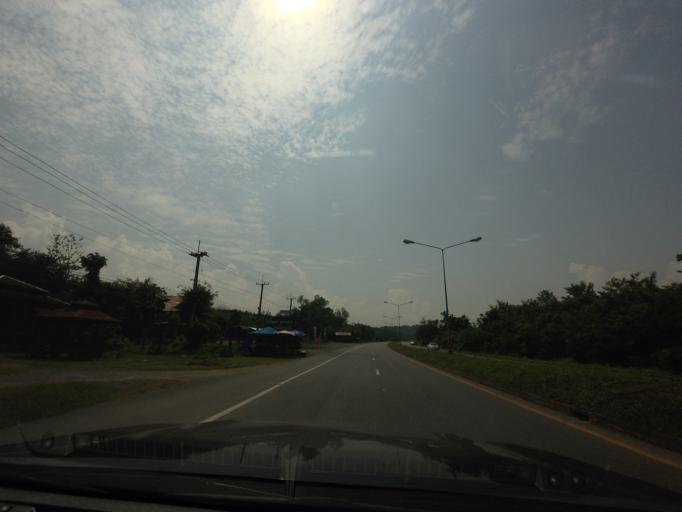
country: TH
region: Phrae
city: Den Chai
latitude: 17.9549
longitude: 100.0683
